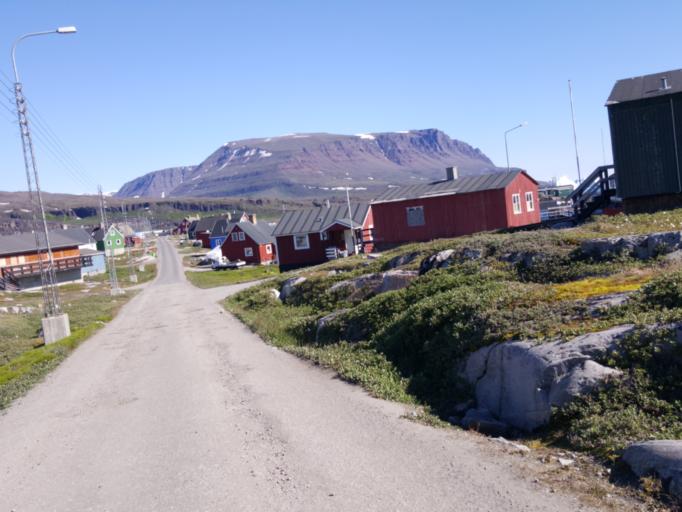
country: GL
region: Qaasuitsup
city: Aasiaat
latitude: 69.2417
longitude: -53.5379
